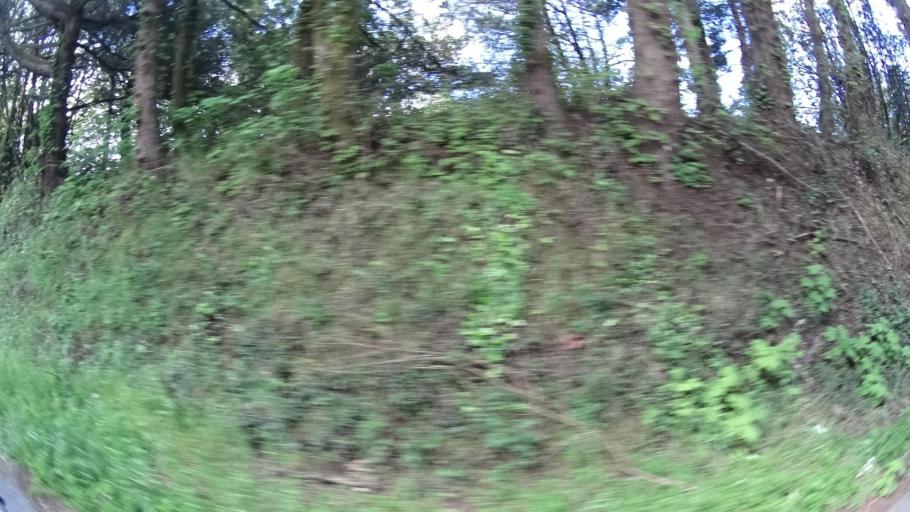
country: US
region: California
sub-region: Humboldt County
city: Blue Lake
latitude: 40.9017
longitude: -124.0284
